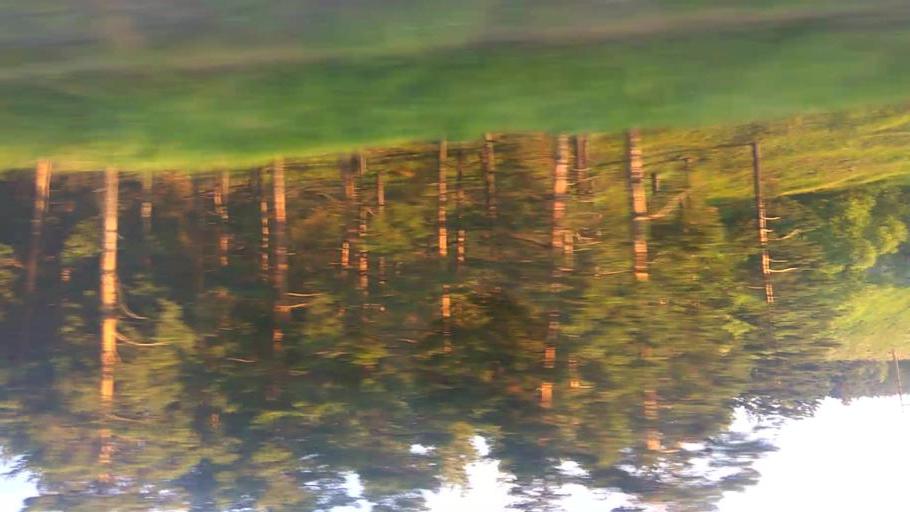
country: RU
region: Moskovskaya
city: Kashira
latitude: 54.8675
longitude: 38.1557
